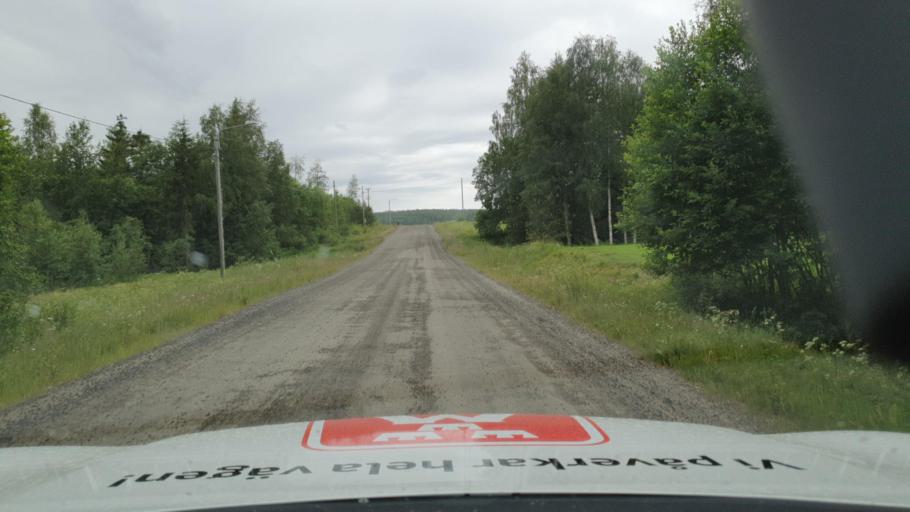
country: SE
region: Vaesterbotten
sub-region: Bjurholms Kommun
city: Bjurholm
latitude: 63.7947
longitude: 19.3306
